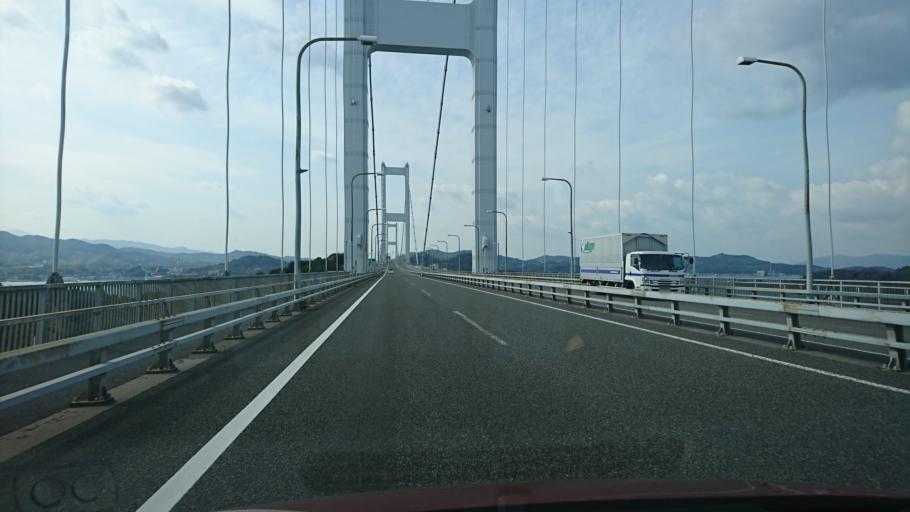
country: JP
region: Hiroshima
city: Takehara
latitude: 34.1196
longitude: 132.9962
